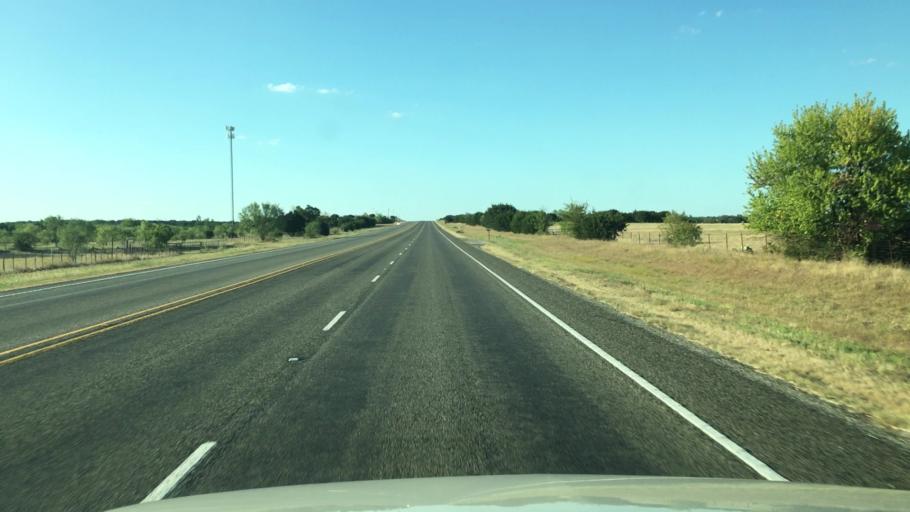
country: US
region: Texas
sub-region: Lampasas County
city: Lampasas
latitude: 31.1772
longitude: -98.1735
